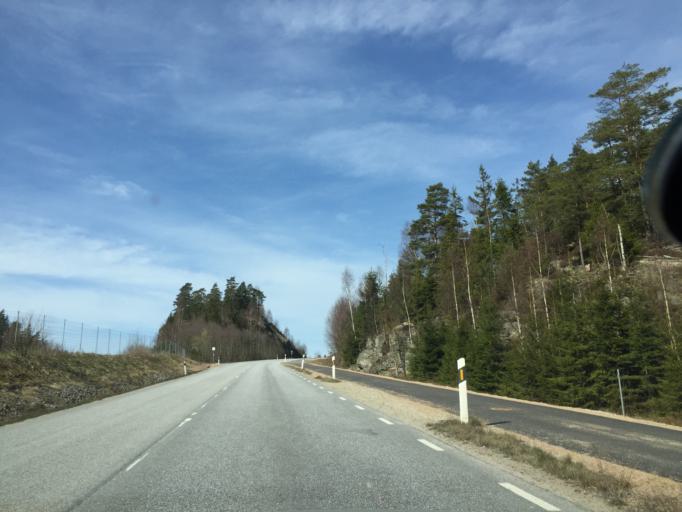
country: SE
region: Vaestra Goetaland
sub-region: Uddevalla Kommun
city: Uddevalla
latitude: 58.3607
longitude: 11.8092
